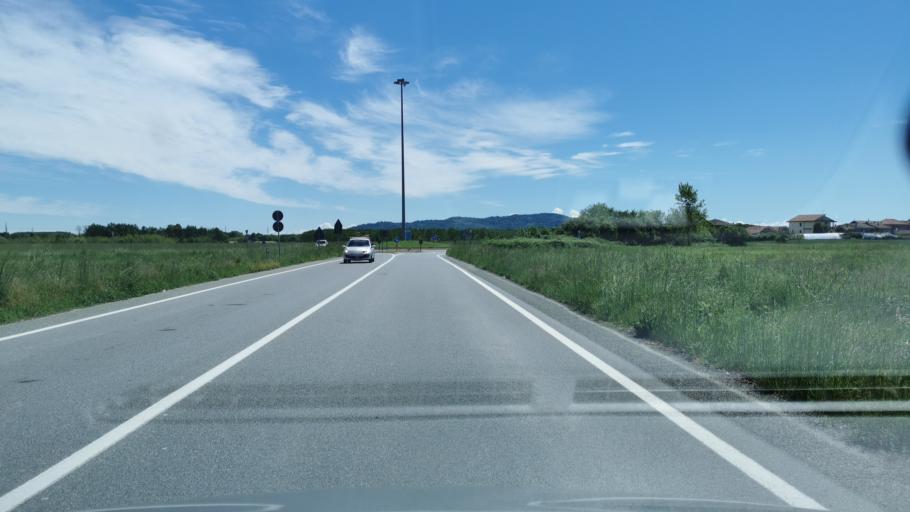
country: IT
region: Piedmont
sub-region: Provincia di Torino
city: Volpiano
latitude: 45.2077
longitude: 7.7878
